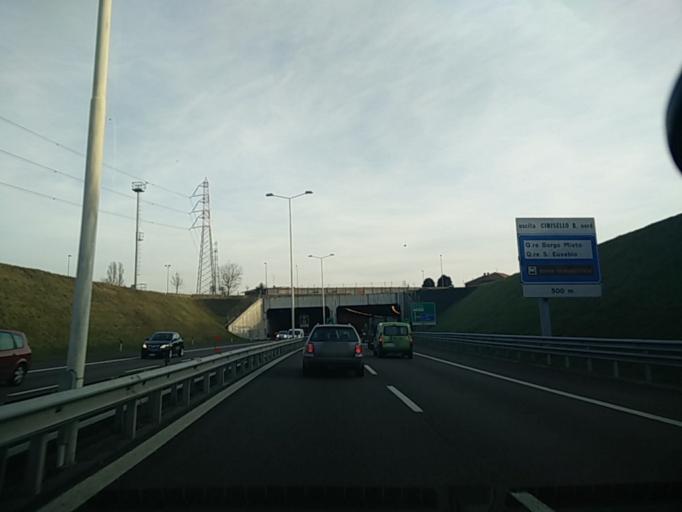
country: IT
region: Lombardy
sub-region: Provincia di Monza e Brianza
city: Muggio
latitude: 45.5748
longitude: 9.2226
